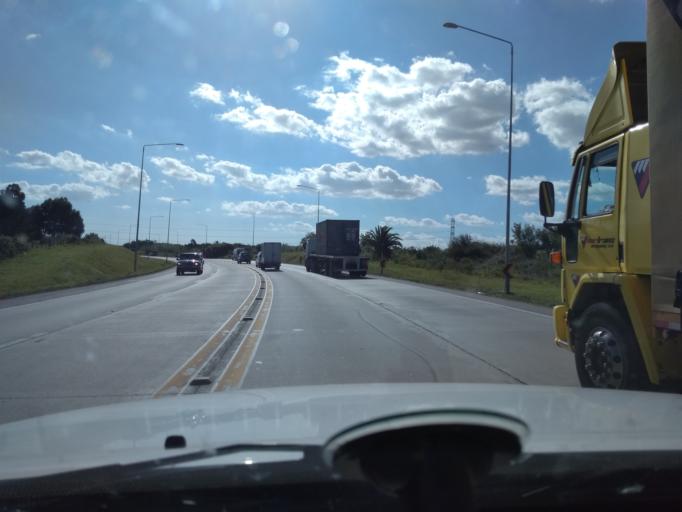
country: UY
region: Canelones
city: La Paz
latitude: -34.7796
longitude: -56.2342
